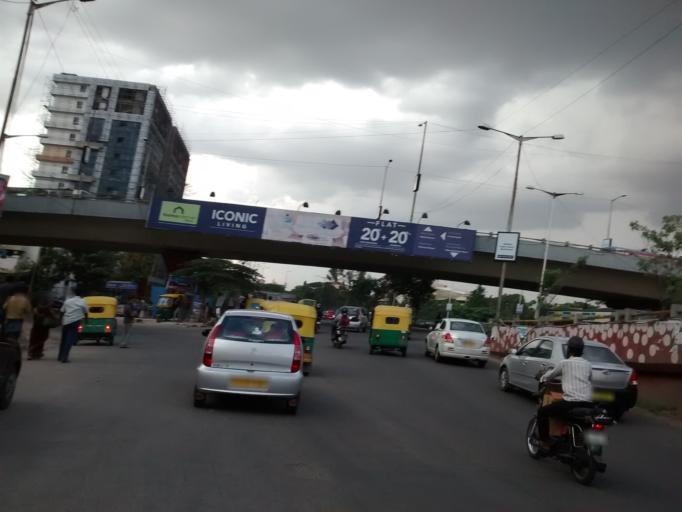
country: IN
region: Karnataka
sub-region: Bangalore Urban
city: Bangalore
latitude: 12.9604
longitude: 77.6422
